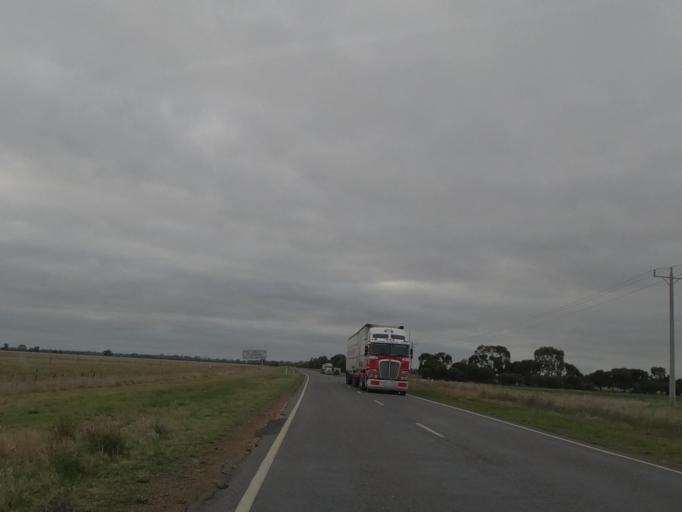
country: AU
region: Victoria
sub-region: Greater Bendigo
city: Long Gully
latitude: -36.4669
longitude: 143.9641
